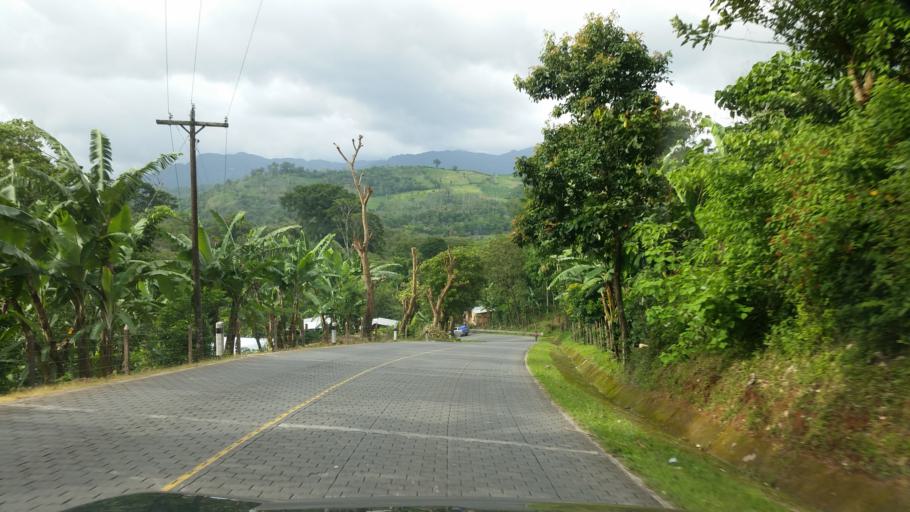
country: NI
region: Jinotega
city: Jinotega
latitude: 13.1858
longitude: -85.7334
